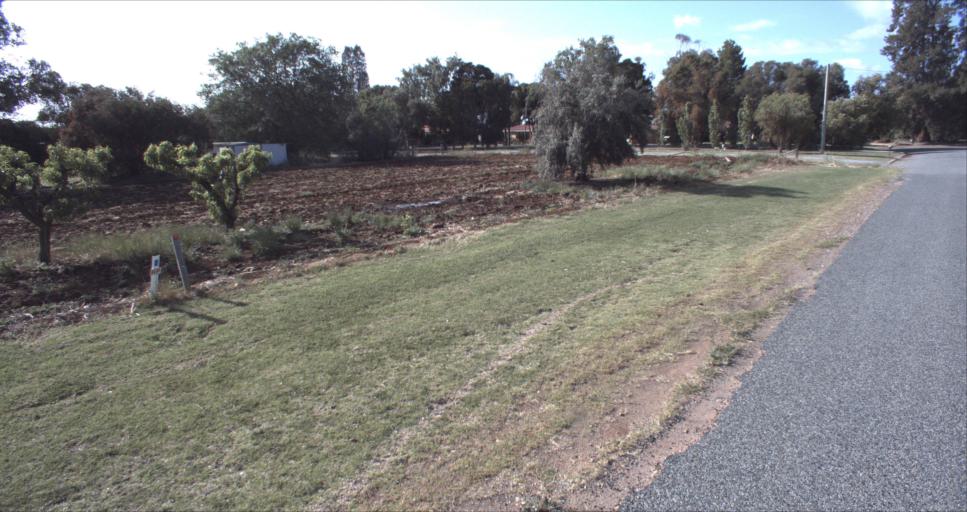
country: AU
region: New South Wales
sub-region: Leeton
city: Leeton
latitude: -34.5690
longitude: 146.3919
